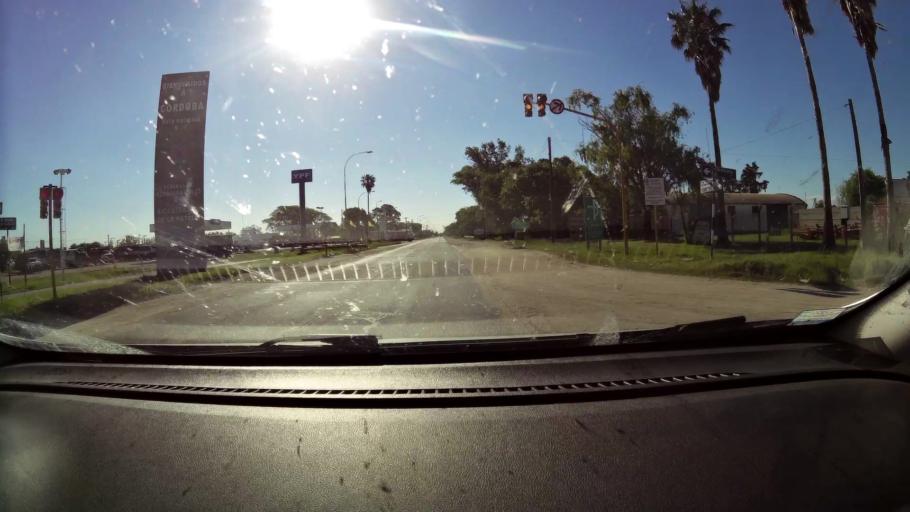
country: AR
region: Cordoba
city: San Francisco
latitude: -31.4202
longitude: -62.0625
